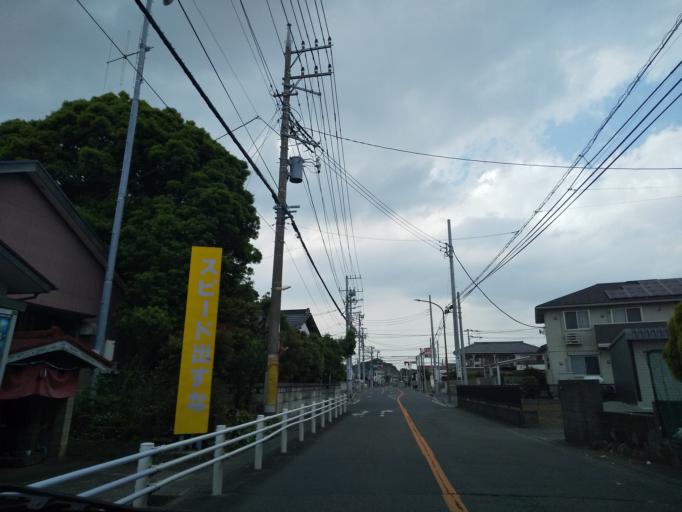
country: JP
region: Tokyo
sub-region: Machida-shi
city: Machida
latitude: 35.5367
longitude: 139.4159
